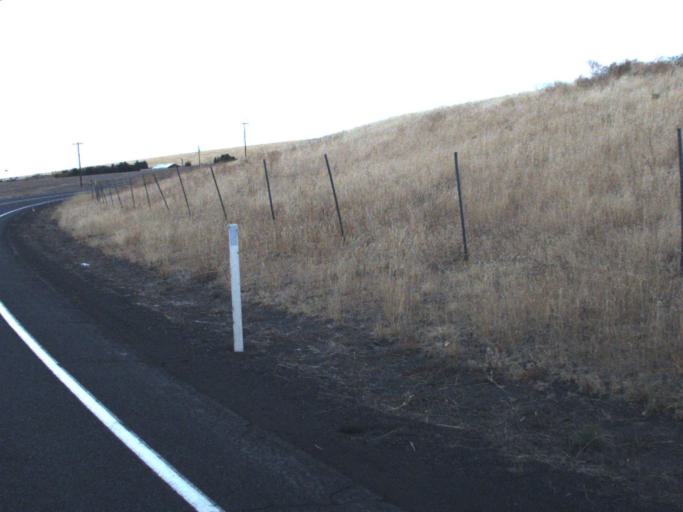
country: US
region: Washington
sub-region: Lincoln County
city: Davenport
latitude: 47.5758
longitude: -117.9392
